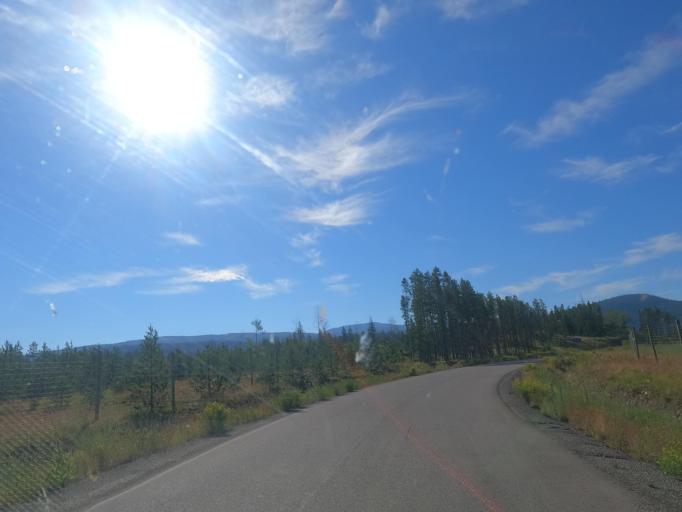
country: CA
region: British Columbia
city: Merritt
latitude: 49.8846
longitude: -120.4660
